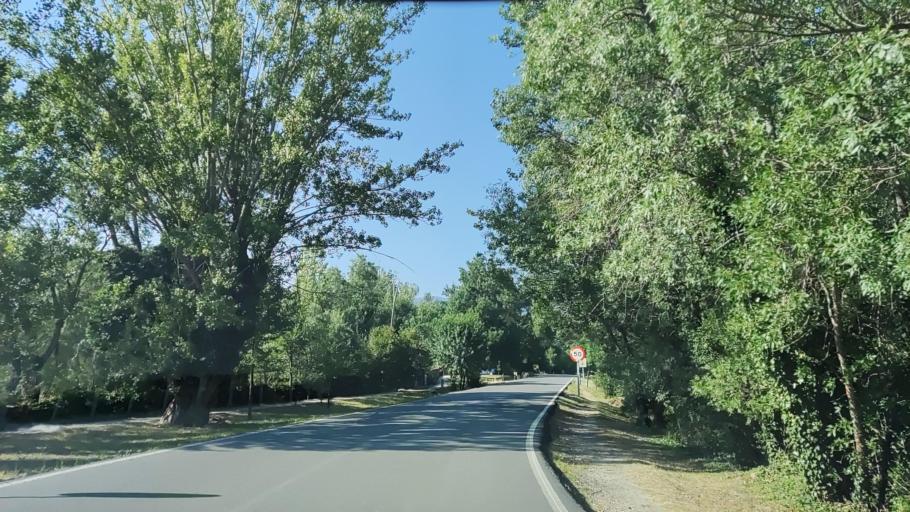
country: ES
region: Madrid
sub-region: Provincia de Madrid
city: Rascafria
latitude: 40.8857
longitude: -3.8873
